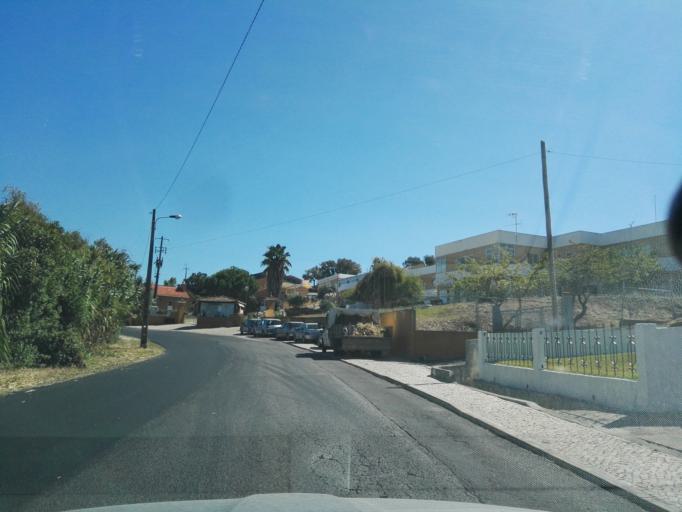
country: PT
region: Lisbon
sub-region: Arruda Dos Vinhos
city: Arruda dos Vinhos
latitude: 38.9781
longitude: -9.0763
